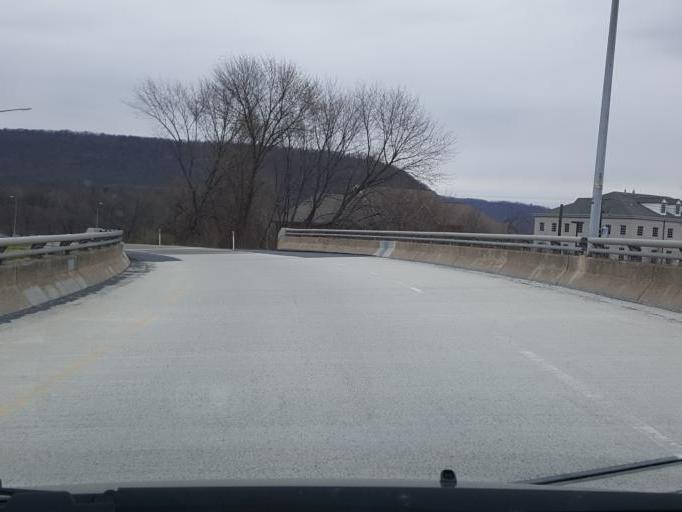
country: US
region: Pennsylvania
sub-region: Dauphin County
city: Harrisburg
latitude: 40.3122
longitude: -76.8983
